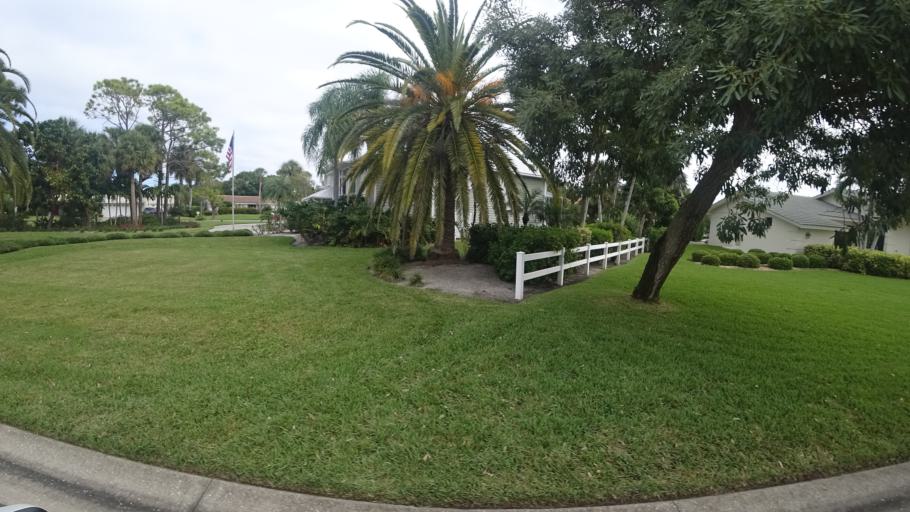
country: US
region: Florida
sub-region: Manatee County
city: Longboat Key
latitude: 27.4212
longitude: -82.6652
